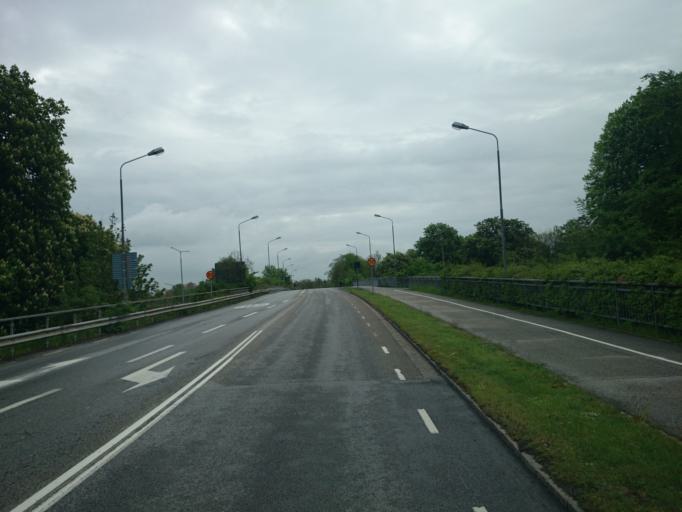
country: SE
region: Skane
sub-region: Burlovs Kommun
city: Arloev
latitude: 55.6097
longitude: 13.0637
